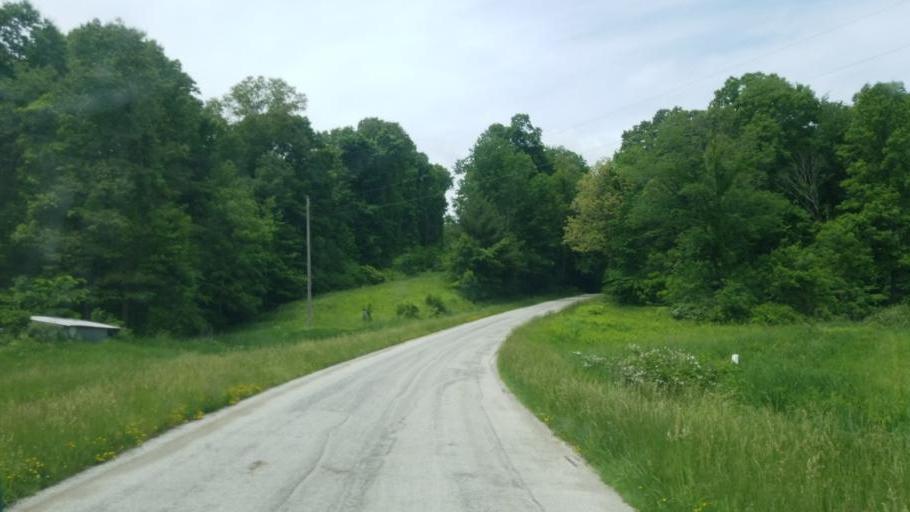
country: US
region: Ohio
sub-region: Coshocton County
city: West Lafayette
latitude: 40.3777
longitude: -81.7873
